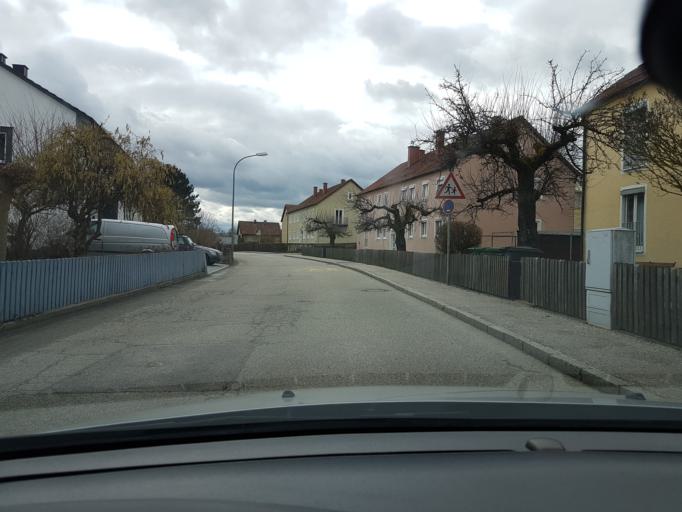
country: DE
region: Bavaria
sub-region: Lower Bavaria
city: Vilsbiburg
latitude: 48.4558
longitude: 12.3561
